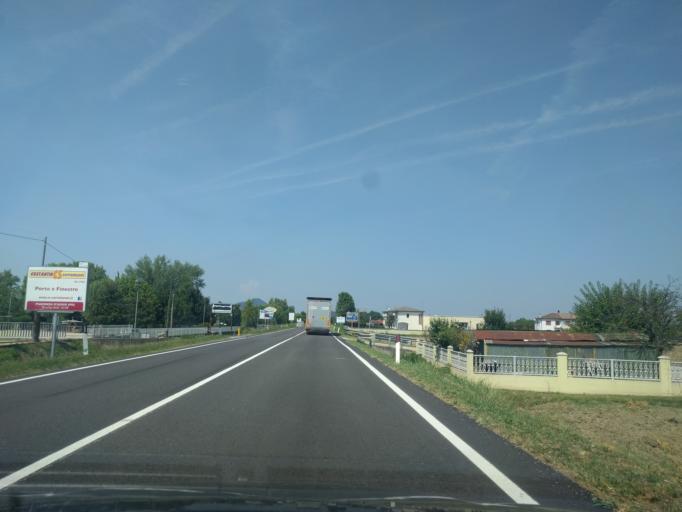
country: IT
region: Veneto
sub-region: Provincia di Padova
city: Solesino
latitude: 45.1874
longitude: 11.7559
